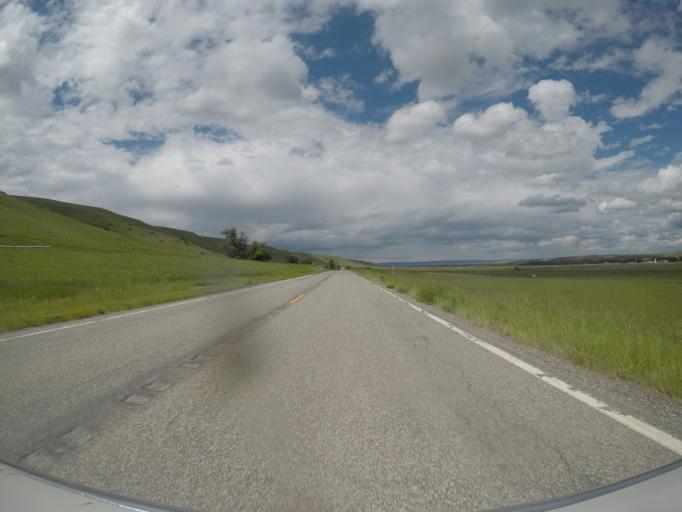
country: US
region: Montana
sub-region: Sweet Grass County
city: Big Timber
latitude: 45.7728
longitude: -109.9888
